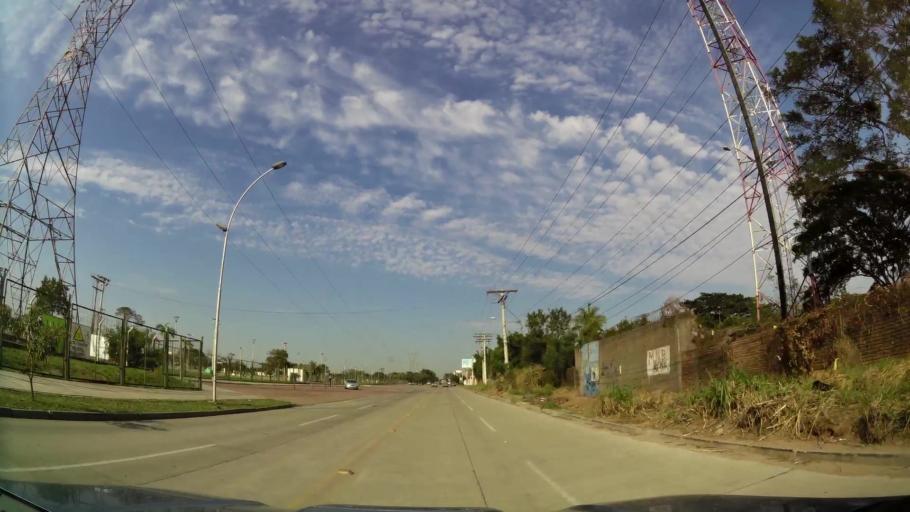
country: BO
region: Santa Cruz
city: Santa Cruz de la Sierra
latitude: -17.7496
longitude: -63.1515
